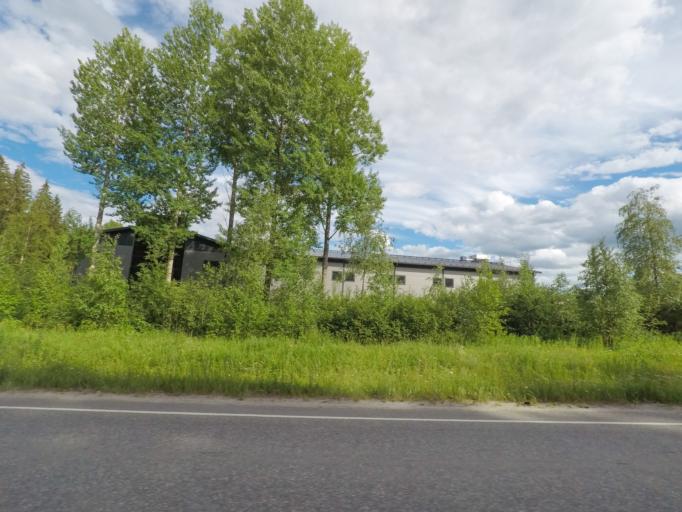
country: FI
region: Paijanne Tavastia
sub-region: Lahti
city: Lahti
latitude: 60.9376
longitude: 25.5933
